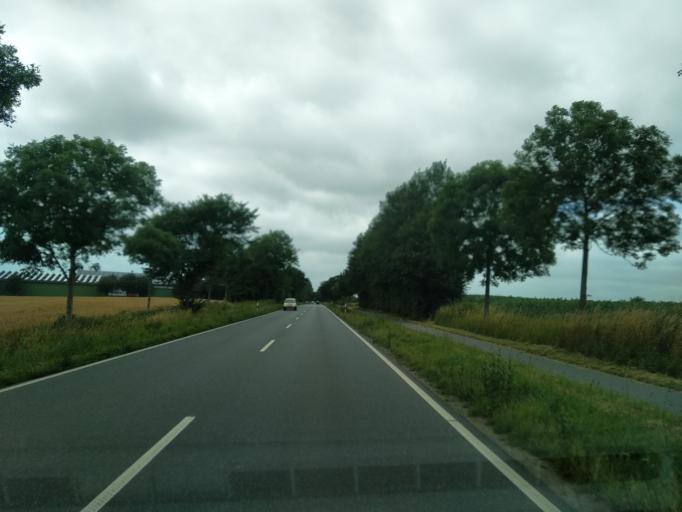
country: DE
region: Schleswig-Holstein
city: Ringsberg
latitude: 54.8020
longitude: 9.6149
